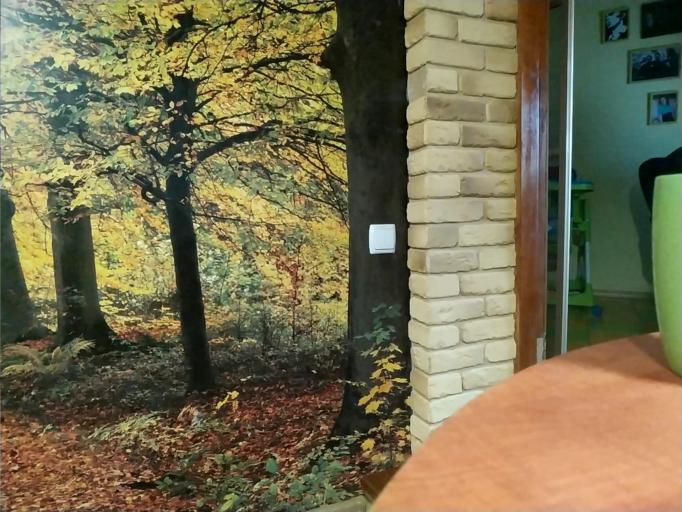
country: RU
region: Tverskaya
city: Staraya Toropa
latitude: 56.3459
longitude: 31.8324
